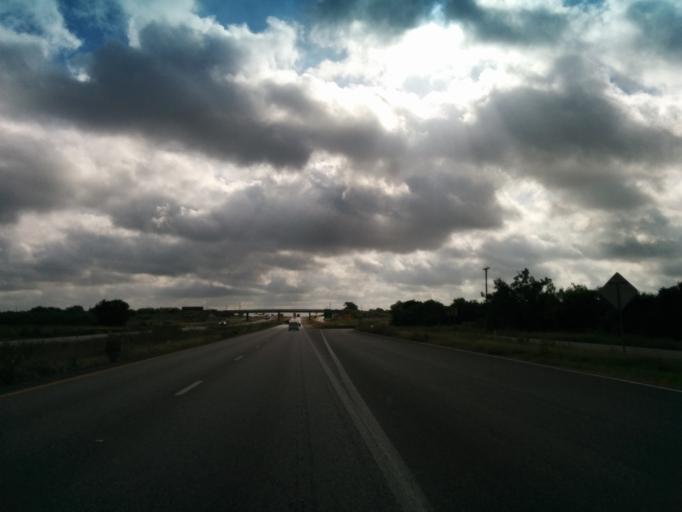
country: US
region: Texas
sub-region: Guadalupe County
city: Marion
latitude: 29.5066
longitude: -98.1716
